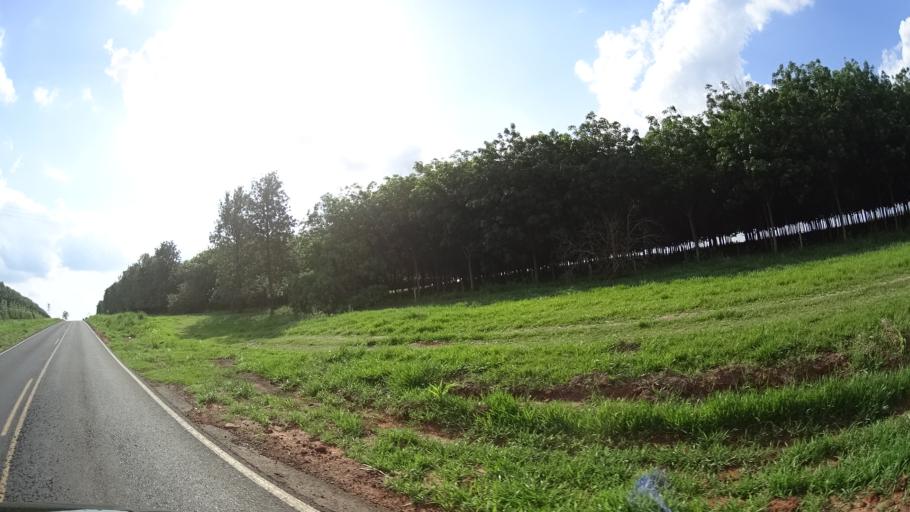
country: BR
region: Sao Paulo
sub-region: Urupes
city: Urupes
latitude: -21.2106
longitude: -49.3389
